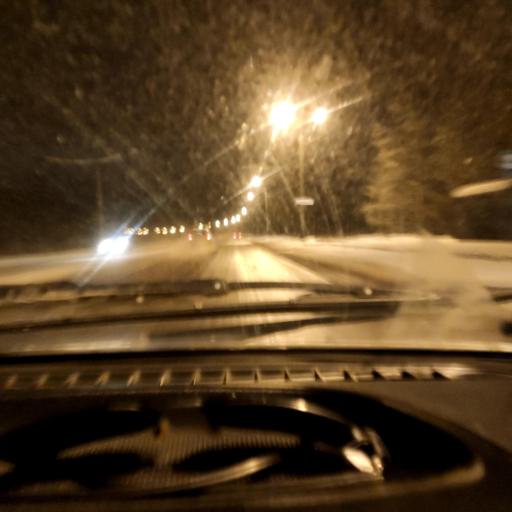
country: RU
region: Samara
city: Zhigulevsk
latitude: 53.4970
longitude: 49.5081
